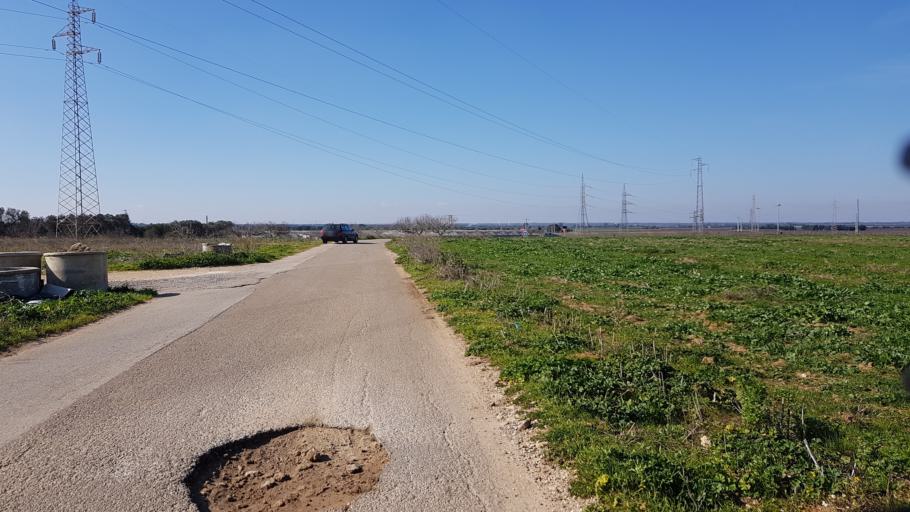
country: IT
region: Apulia
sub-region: Provincia di Brindisi
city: Mesagne
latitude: 40.6207
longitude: 17.8234
